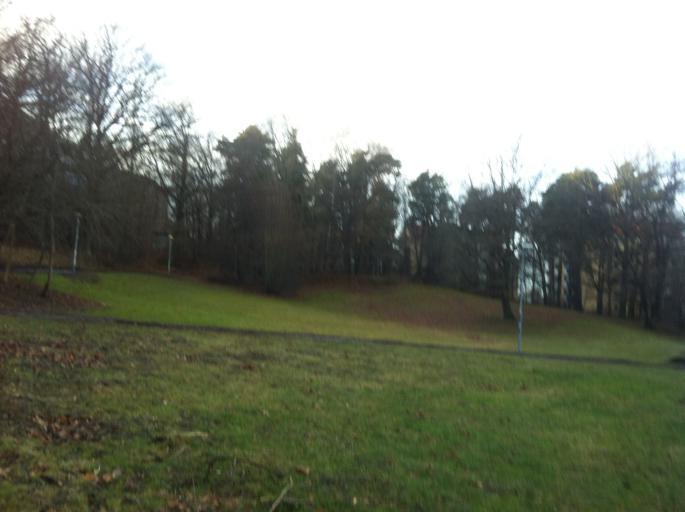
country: SE
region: Stockholm
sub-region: Solna Kommun
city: Solna
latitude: 59.3684
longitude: 18.0029
